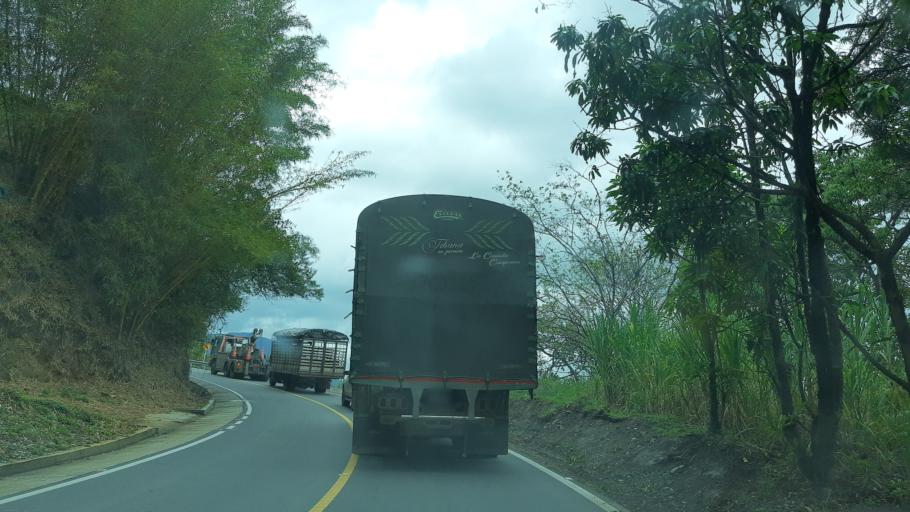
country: CO
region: Boyaca
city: Somondoco
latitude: 4.9795
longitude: -73.3407
